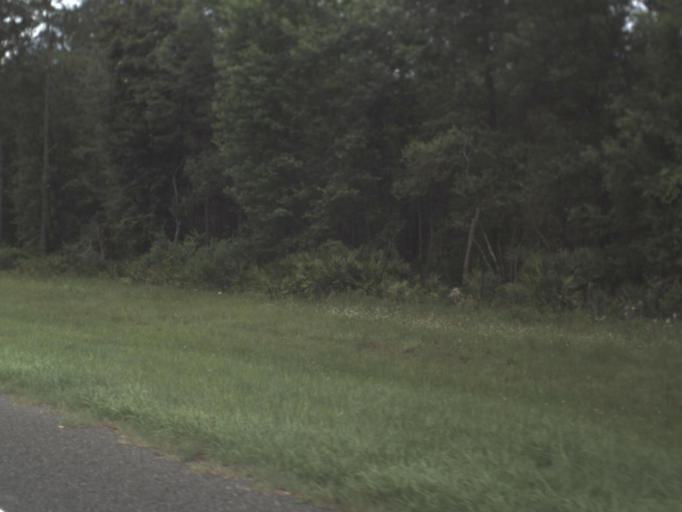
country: US
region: Florida
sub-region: Nassau County
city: Hilliard
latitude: 30.7394
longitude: -81.9513
